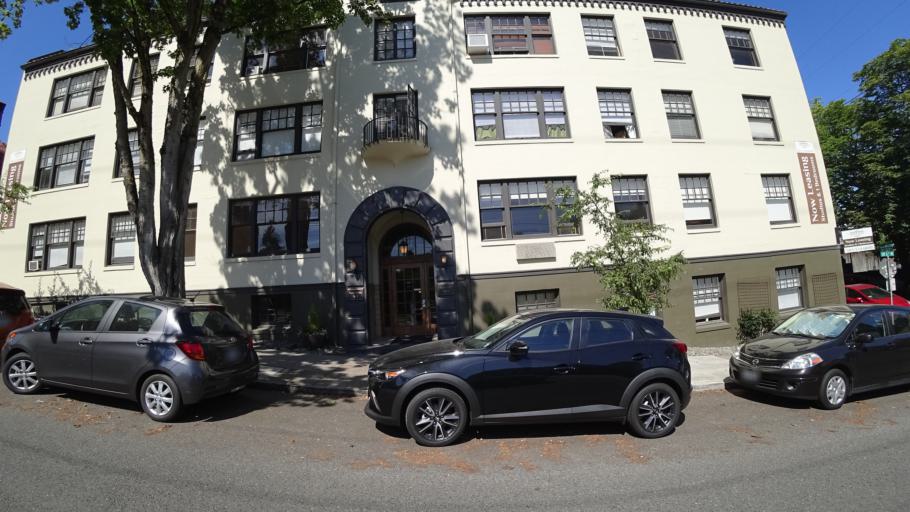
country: US
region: Oregon
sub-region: Multnomah County
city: Portland
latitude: 45.5216
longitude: -122.6942
